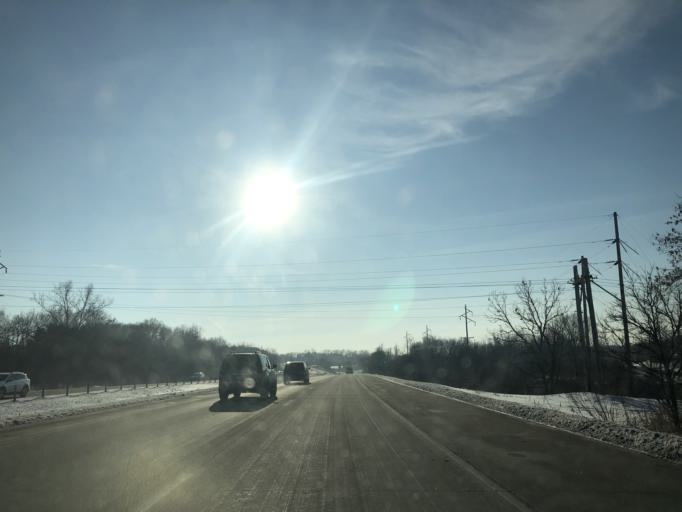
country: US
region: Minnesota
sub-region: Ramsey County
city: Shoreview
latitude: 45.0725
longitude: -93.1694
